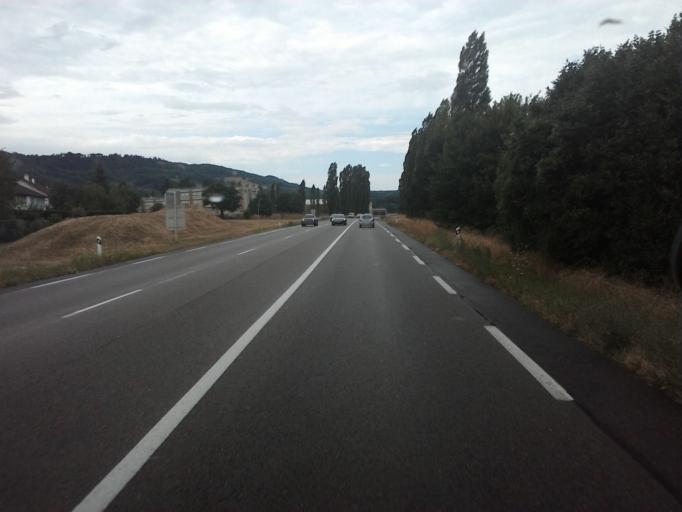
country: FR
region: Franche-Comte
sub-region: Departement du Jura
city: Poligny
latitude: 46.8403
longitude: 5.6988
